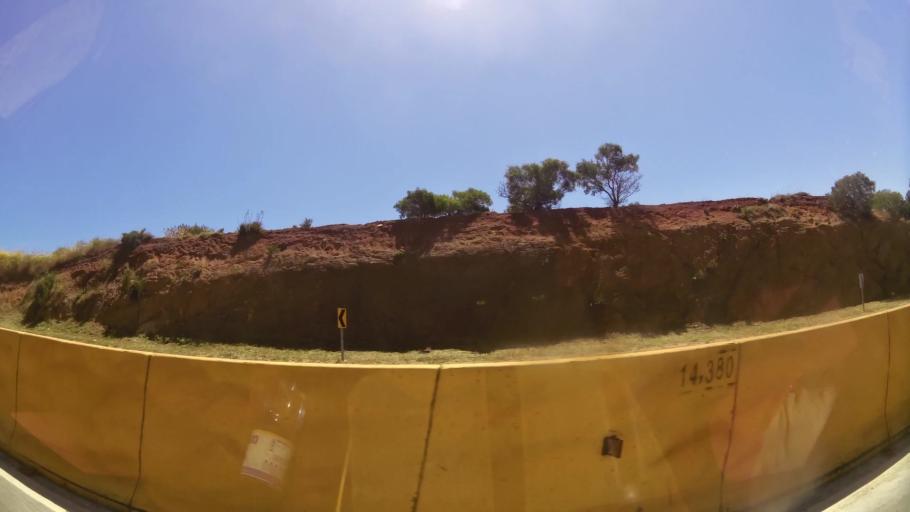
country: CL
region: Valparaiso
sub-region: Provincia de Valparaiso
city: Valparaiso
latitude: -33.0478
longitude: -71.6574
